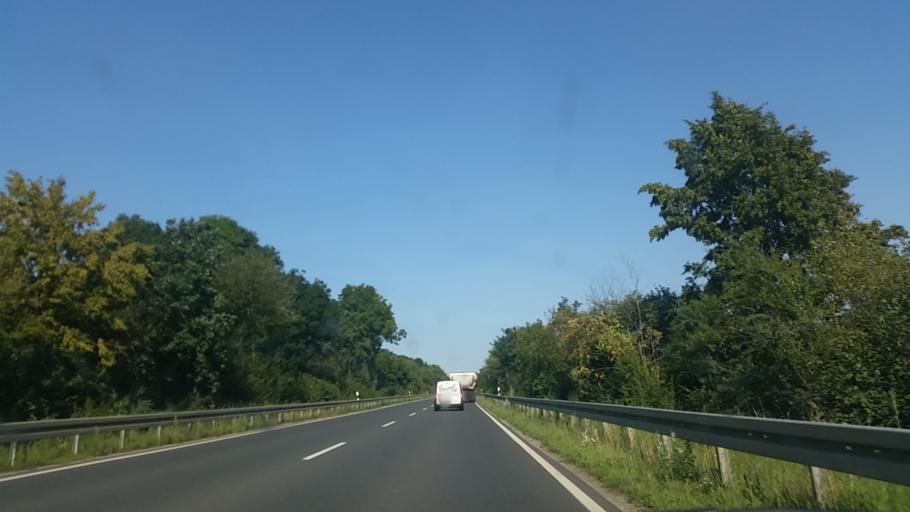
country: DE
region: Lower Saxony
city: Coppenbrugge
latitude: 52.1180
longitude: 9.5216
